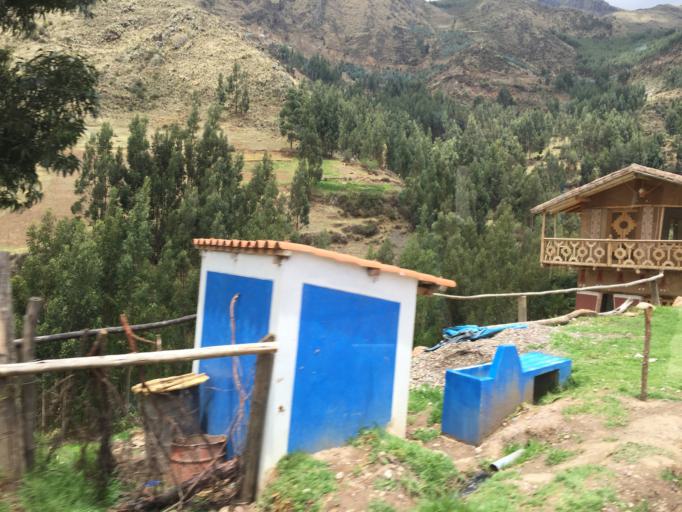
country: PE
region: Cusco
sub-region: Provincia de Calca
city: Pisac
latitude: -13.4102
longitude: -71.8362
